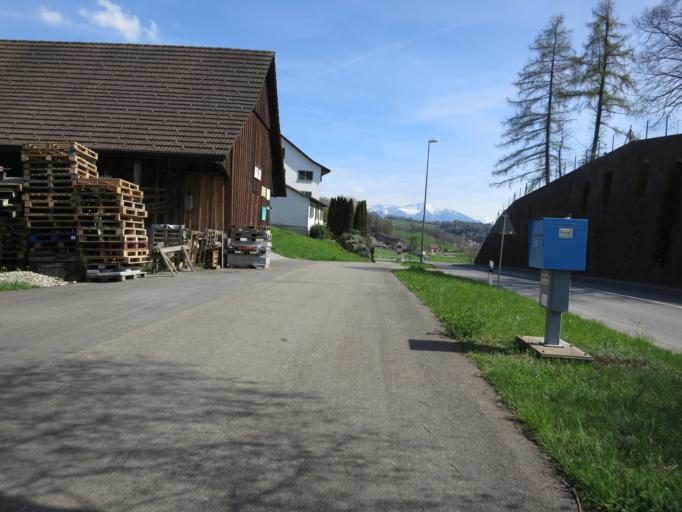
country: CH
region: Zurich
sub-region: Bezirk Hinwil
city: Rueti / Oberdorf
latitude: 47.2521
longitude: 8.8714
